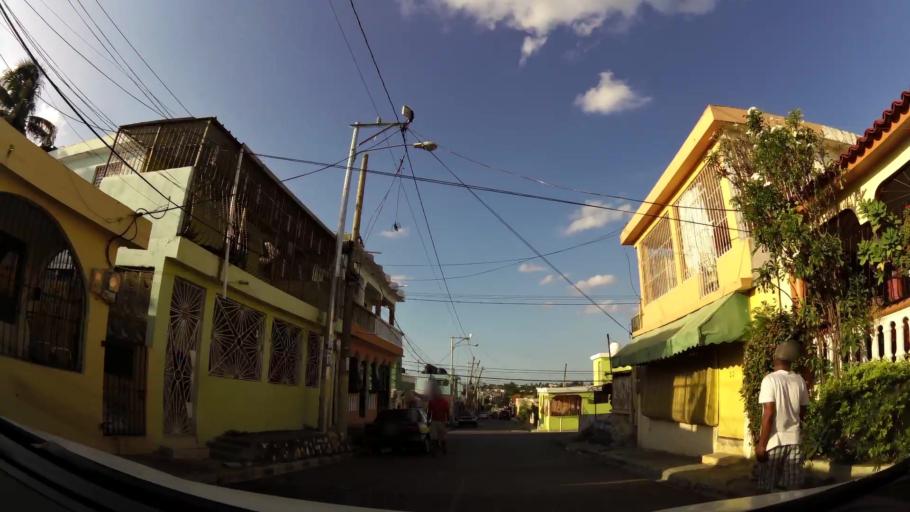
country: DO
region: Nacional
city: Ensanche Luperon
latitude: 18.5435
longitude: -69.9075
